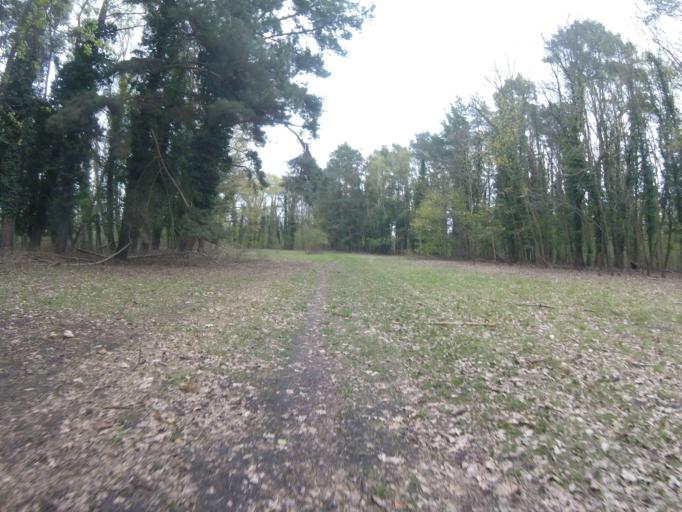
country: DE
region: Brandenburg
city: Bestensee
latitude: 52.2288
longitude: 13.6585
